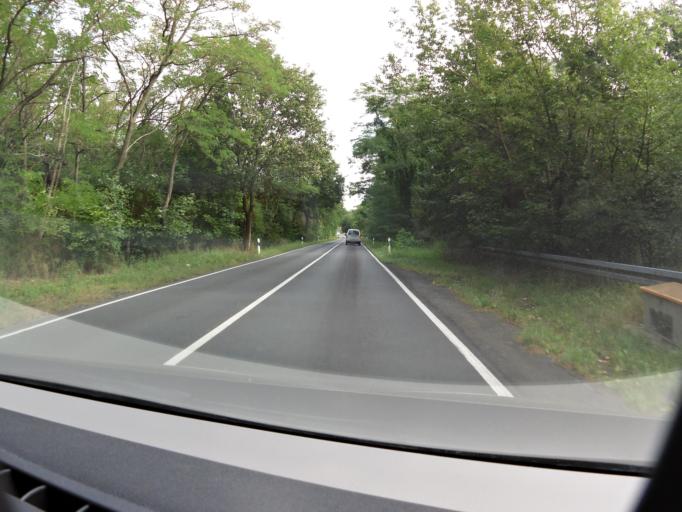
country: DE
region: Brandenburg
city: Furstenwalde
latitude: 52.3440
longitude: 14.0449
